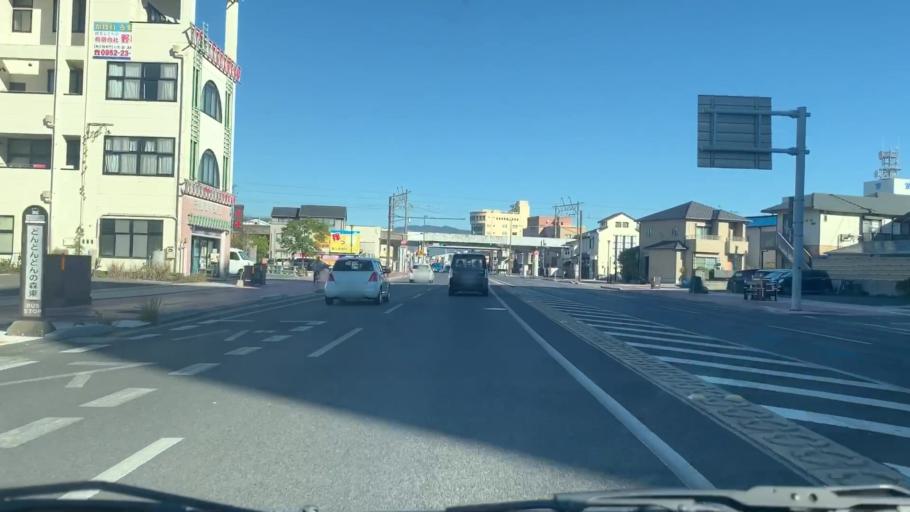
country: JP
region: Saga Prefecture
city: Saga-shi
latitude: 33.2621
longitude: 130.2933
